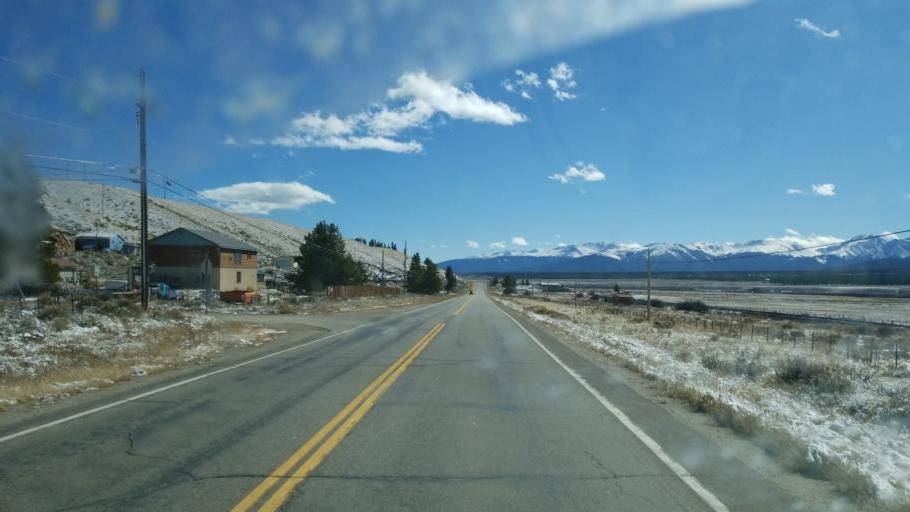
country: US
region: Colorado
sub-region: Lake County
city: Leadville North
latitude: 39.2126
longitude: -106.3465
